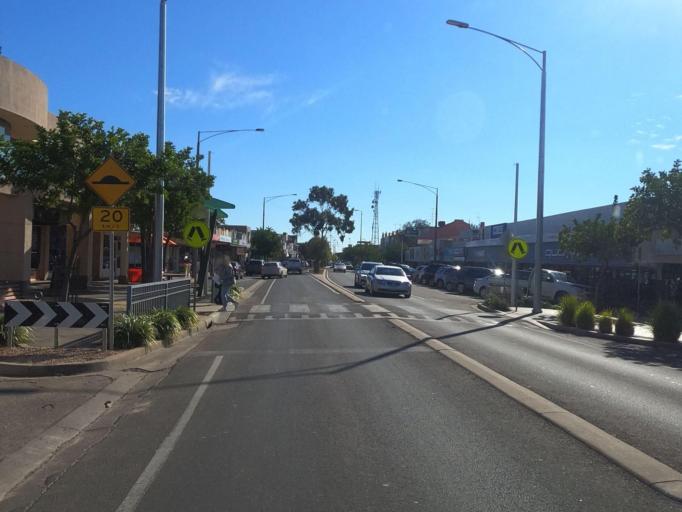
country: AU
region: Victoria
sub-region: Swan Hill
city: Swan Hill
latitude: -35.3419
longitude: 143.5603
